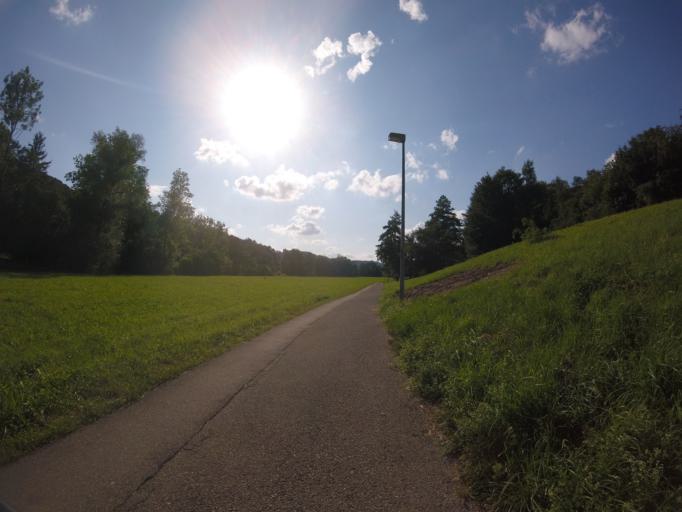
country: DE
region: Baden-Wuerttemberg
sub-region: Regierungsbezirk Stuttgart
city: Murrhardt
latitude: 48.9763
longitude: 9.5973
